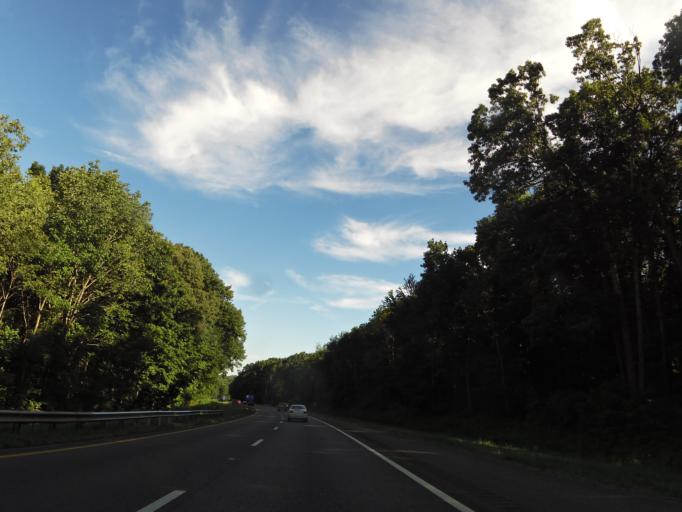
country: US
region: Tennessee
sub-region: Montgomery County
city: Clarksville
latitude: 36.5495
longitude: -87.2468
